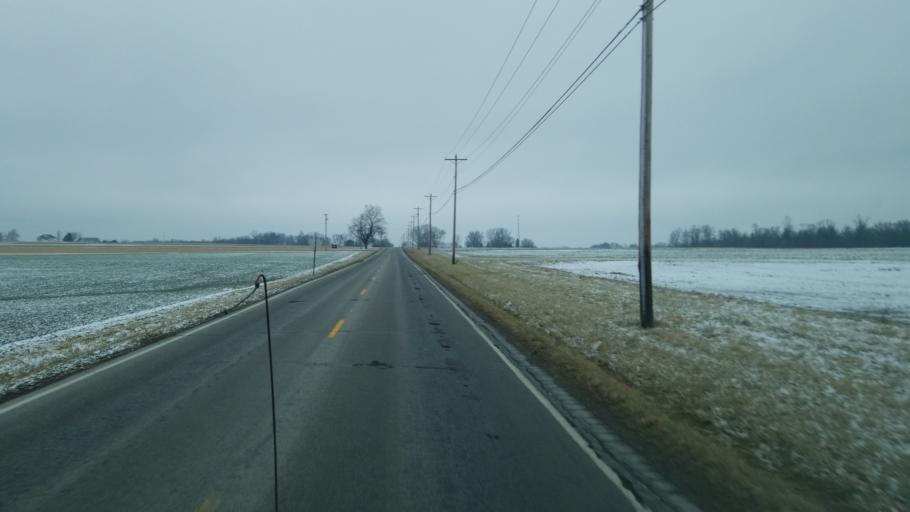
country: US
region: Ohio
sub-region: Wayne County
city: Apple Creek
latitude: 40.7789
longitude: -81.8439
